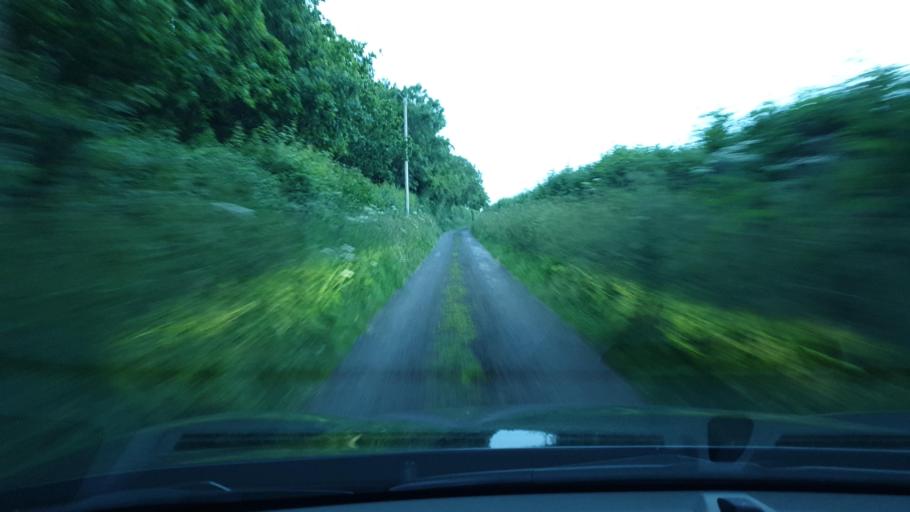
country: IE
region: Leinster
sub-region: An Mhi
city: Duleek
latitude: 53.5954
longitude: -6.3636
